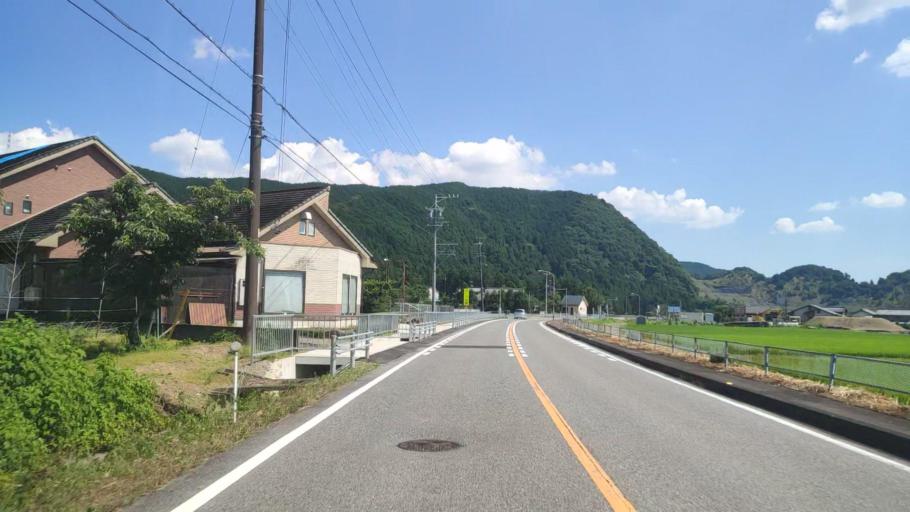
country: JP
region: Gifu
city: Godo
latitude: 35.5360
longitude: 136.6505
